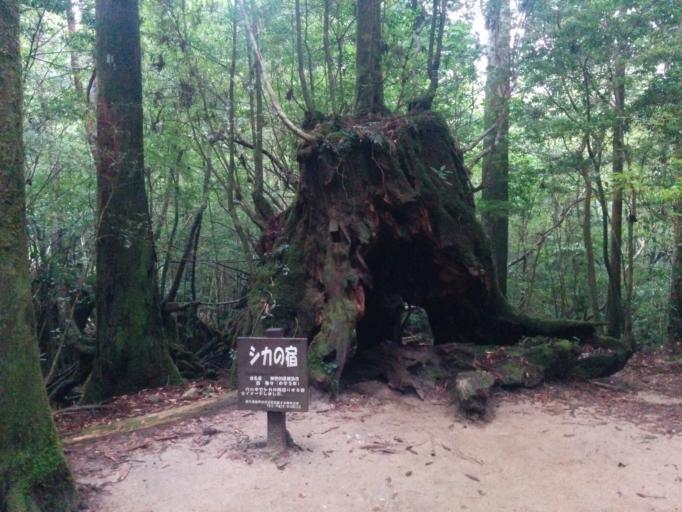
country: JP
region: Kagoshima
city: Nishinoomote
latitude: 30.3698
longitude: 130.5707
